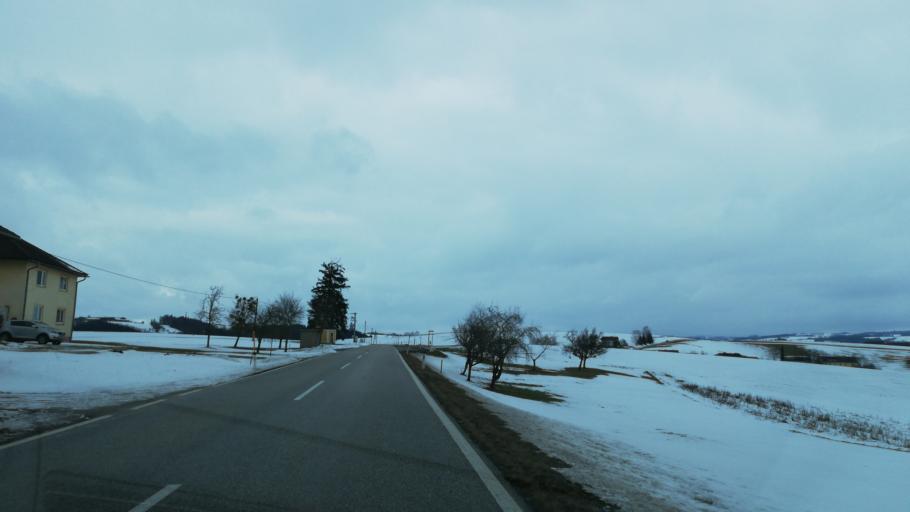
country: AT
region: Upper Austria
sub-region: Politischer Bezirk Urfahr-Umgebung
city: Herzogsdorf
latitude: 48.4056
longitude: 14.0869
